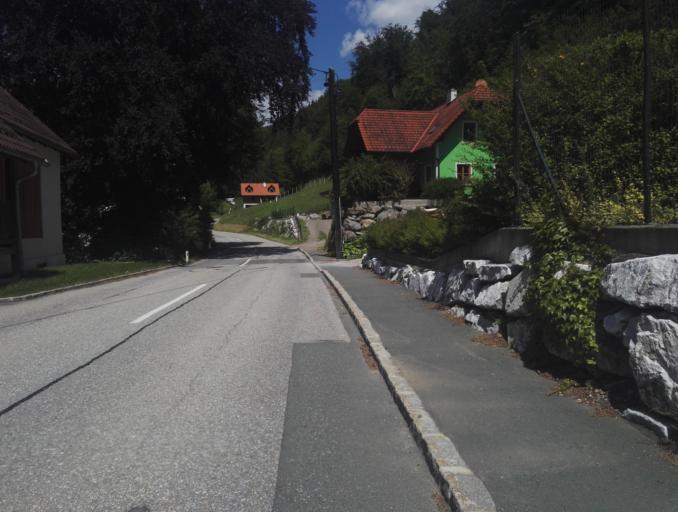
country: AT
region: Styria
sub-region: Politischer Bezirk Graz-Umgebung
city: Deutschfeistritz
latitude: 47.2138
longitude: 15.3104
